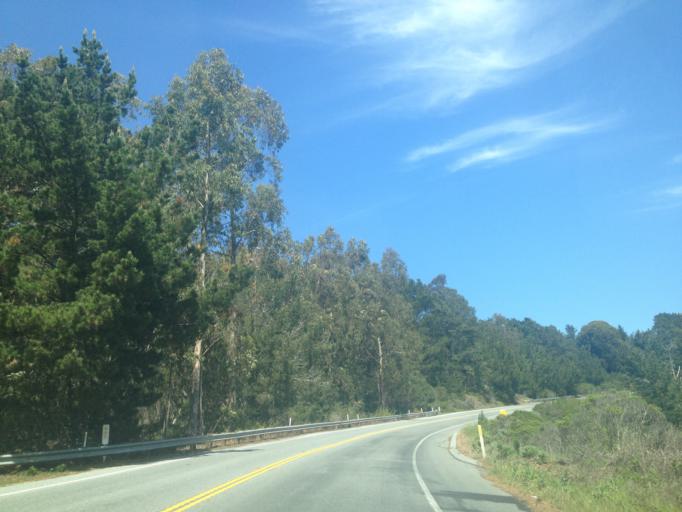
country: US
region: California
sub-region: San Mateo County
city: Half Moon Bay
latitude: 37.3155
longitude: -122.4033
